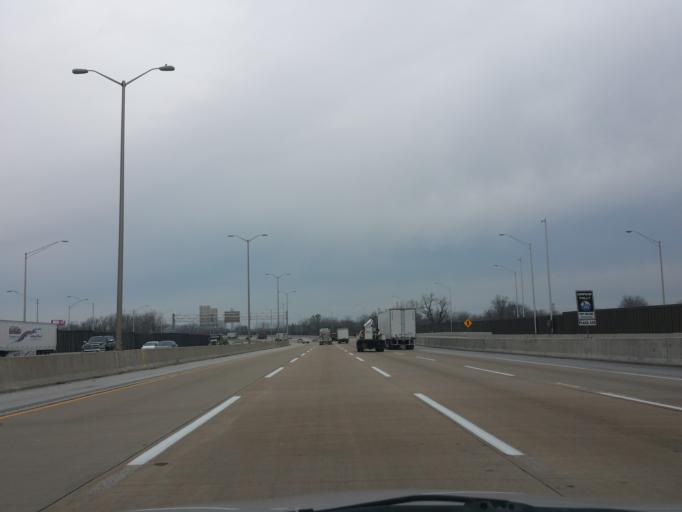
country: US
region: Illinois
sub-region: Cook County
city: Posen
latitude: 41.6267
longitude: -87.6916
